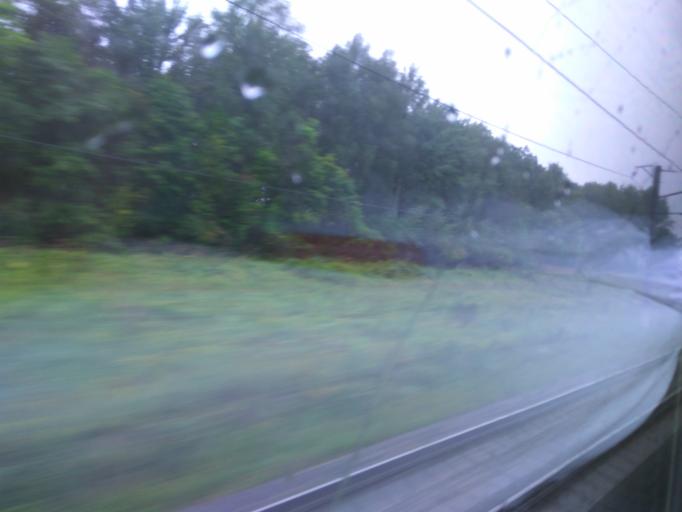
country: RU
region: Moskovskaya
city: Kashira
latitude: 54.8449
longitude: 38.2301
